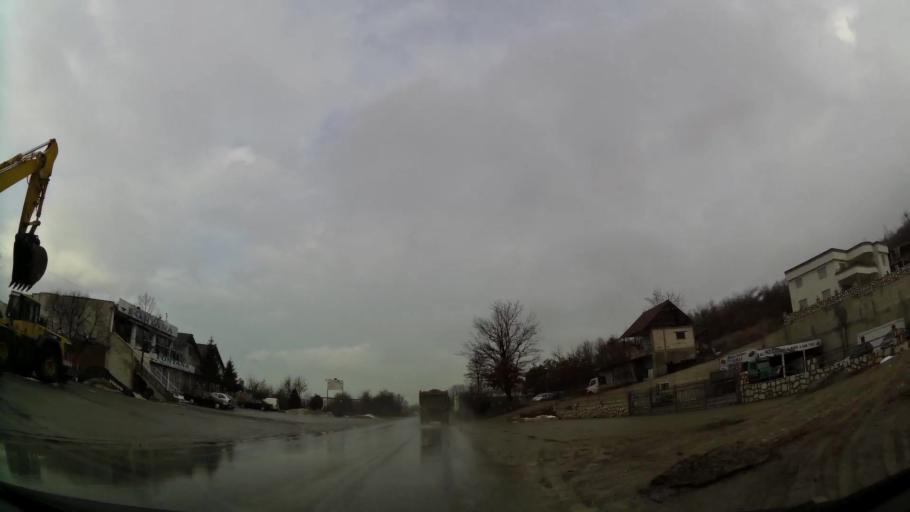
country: XK
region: Ferizaj
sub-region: Komuna e Kacanikut
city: Kacanik
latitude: 42.2488
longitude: 21.2382
